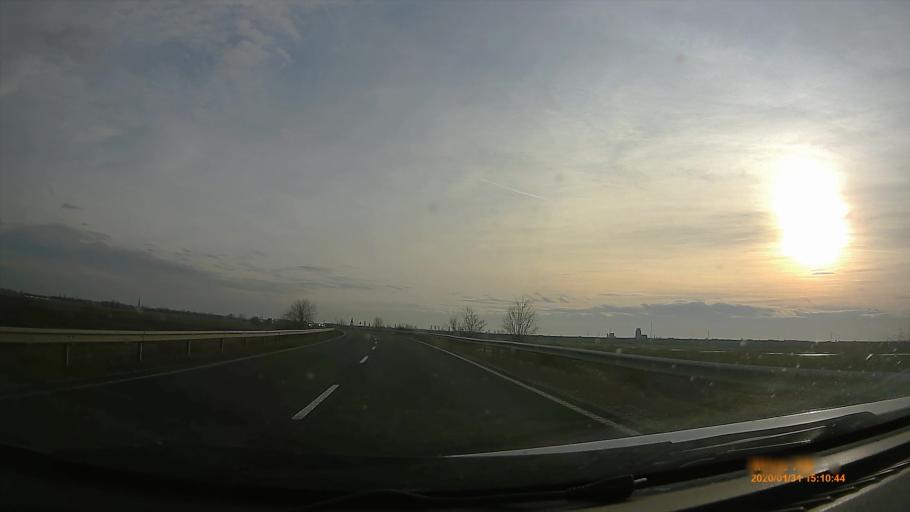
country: HU
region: Hajdu-Bihar
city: Polgar
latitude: 47.8580
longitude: 21.1505
